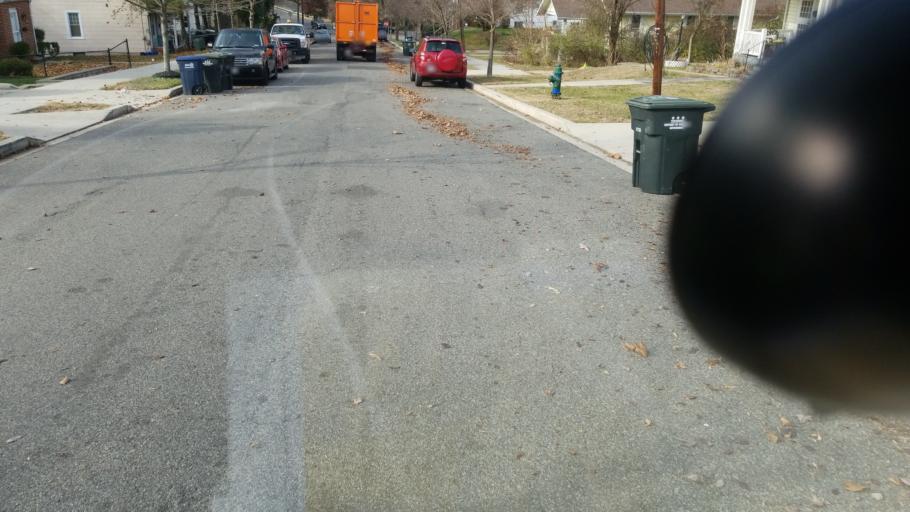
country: US
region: Maryland
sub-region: Prince George's County
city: Silver Hill
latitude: 38.8757
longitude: -76.9595
